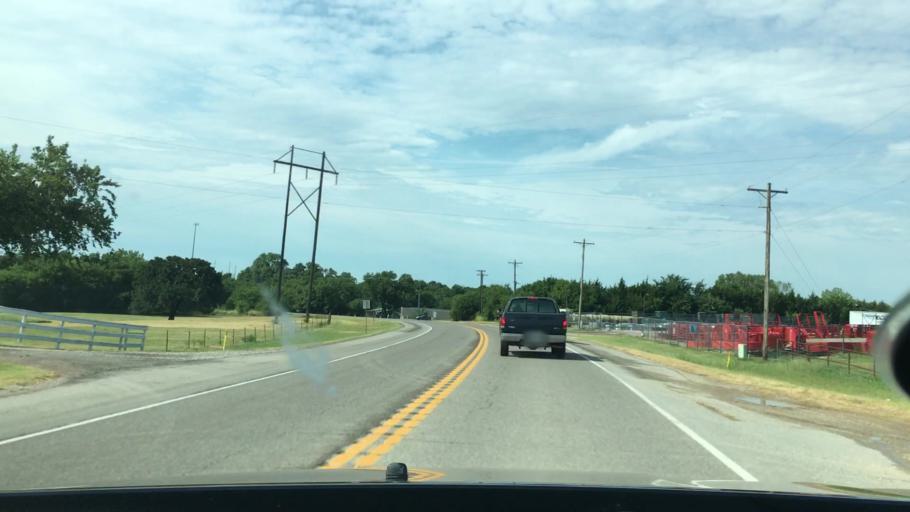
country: US
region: Oklahoma
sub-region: Murray County
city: Sulphur
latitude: 34.5285
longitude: -96.9692
